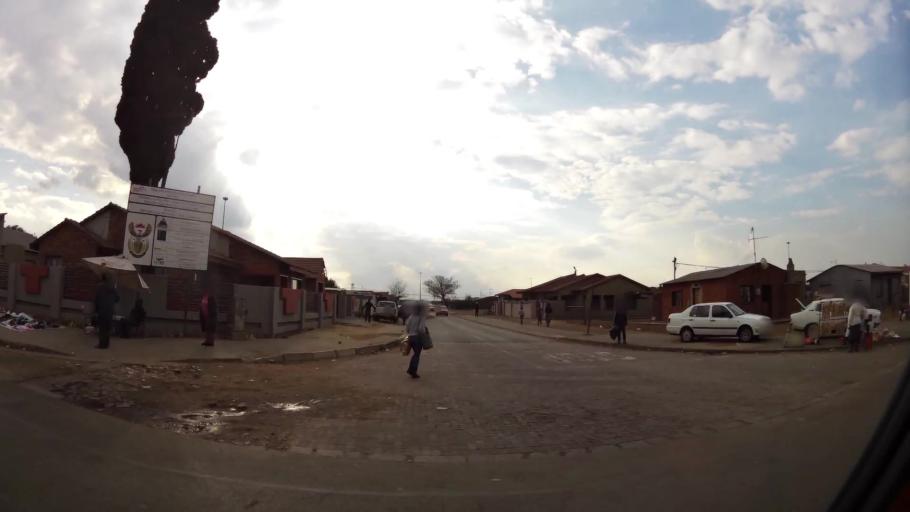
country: ZA
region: Gauteng
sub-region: Sedibeng District Municipality
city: Vanderbijlpark
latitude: -26.6864
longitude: 27.8710
